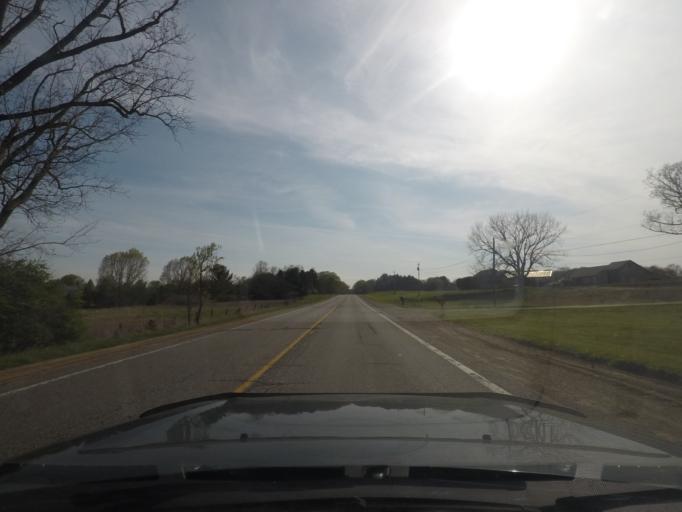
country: US
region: Michigan
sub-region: Berrien County
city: Buchanan
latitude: 41.7992
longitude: -86.4102
